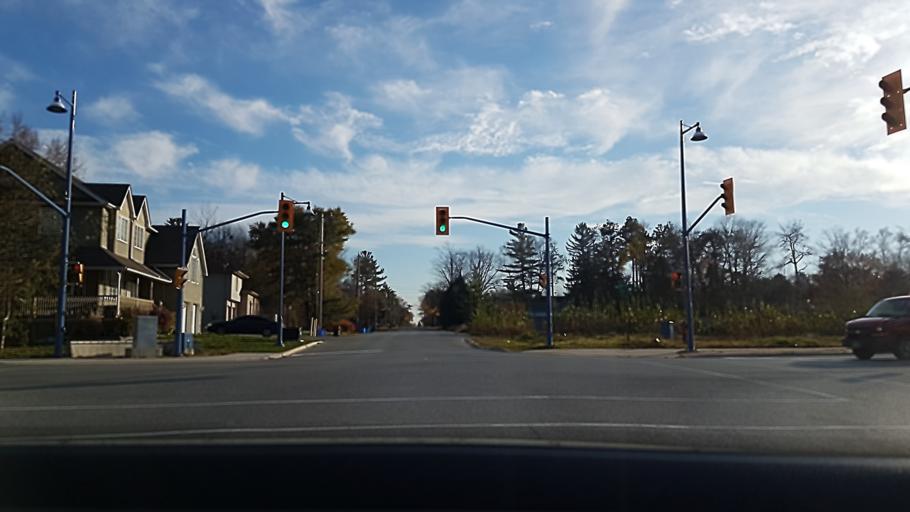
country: CA
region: Ontario
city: Keswick
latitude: 44.3169
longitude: -79.5400
